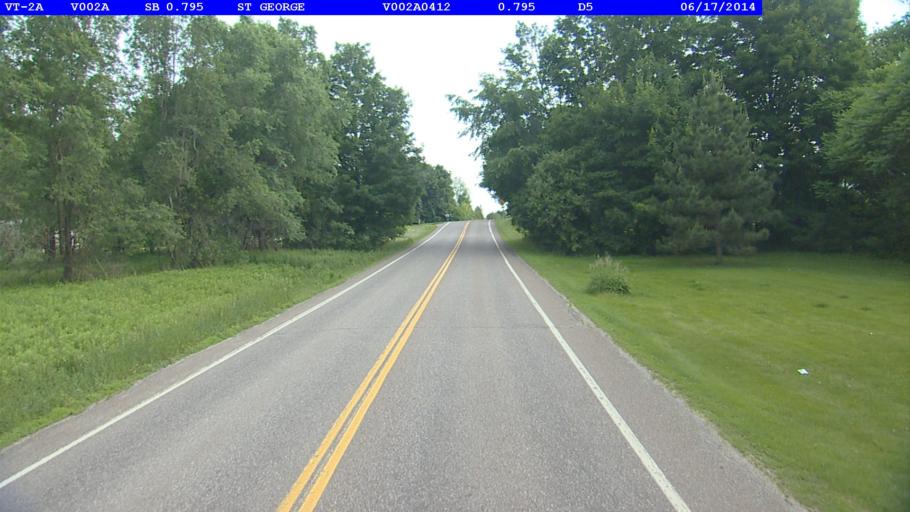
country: US
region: Vermont
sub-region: Chittenden County
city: Hinesburg
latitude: 44.3810
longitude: -73.1262
